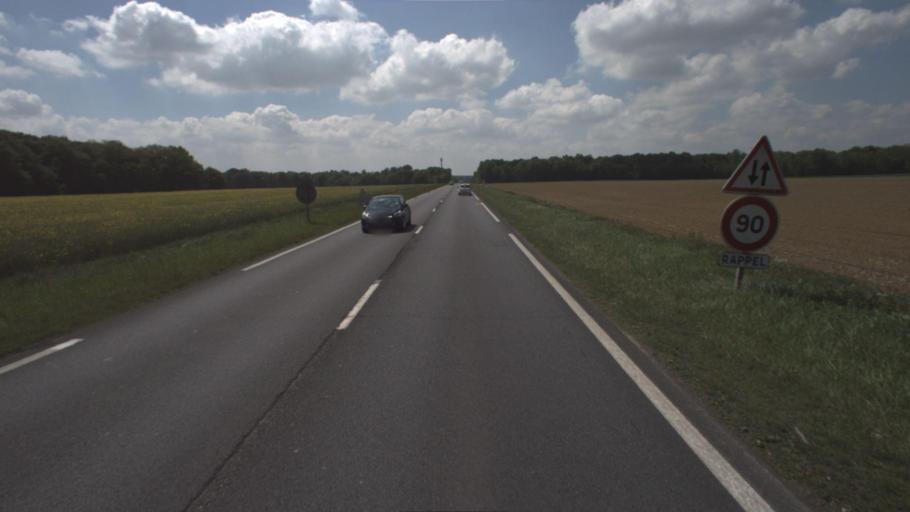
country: FR
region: Ile-de-France
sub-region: Departement de Seine-et-Marne
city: Chaumes-en-Brie
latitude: 48.6741
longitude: 2.8129
